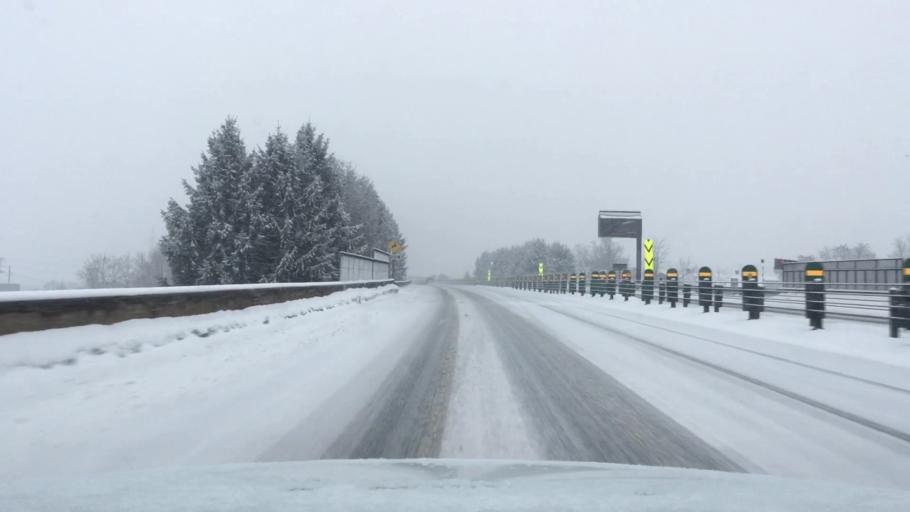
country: JP
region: Akita
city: Hanawa
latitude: 40.2599
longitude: 140.7671
